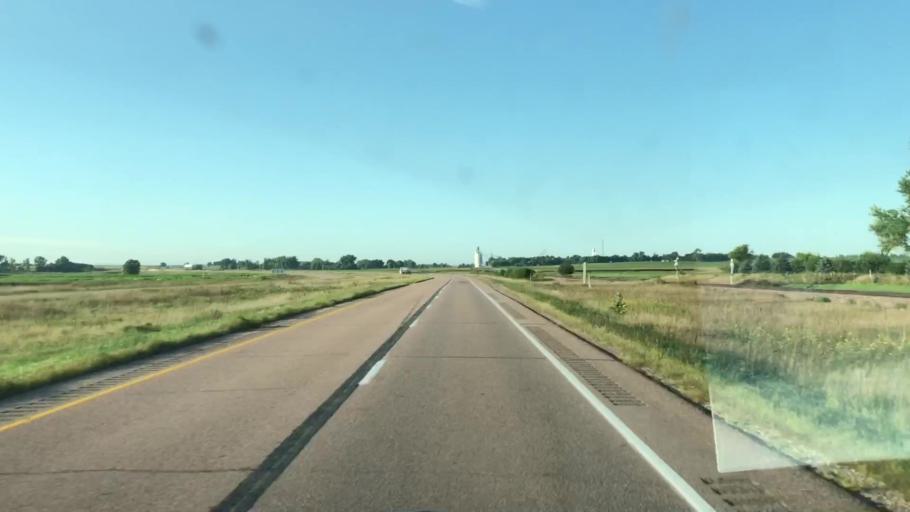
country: US
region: Iowa
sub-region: Osceola County
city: Sibley
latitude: 43.3330
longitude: -95.7792
